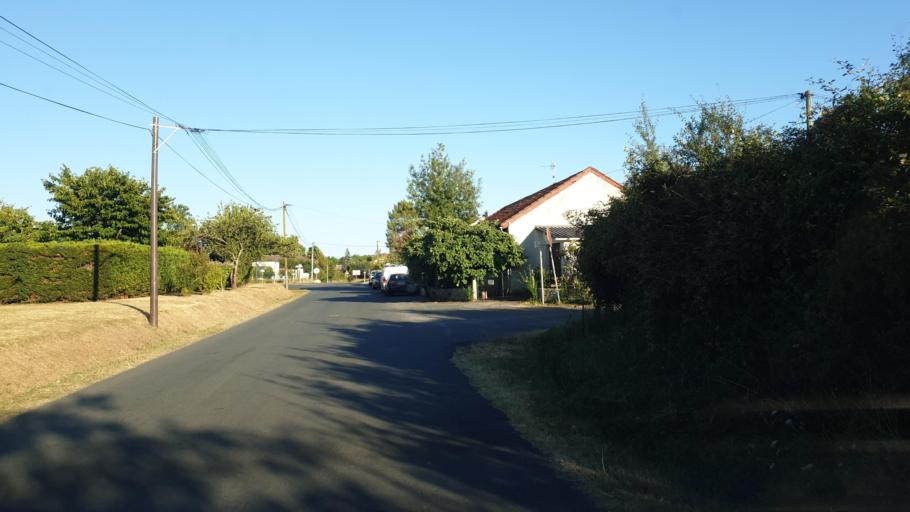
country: FR
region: Aquitaine
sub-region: Departement du Lot-et-Garonne
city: Castelmoron-sur-Lot
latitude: 44.3936
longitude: 0.5010
